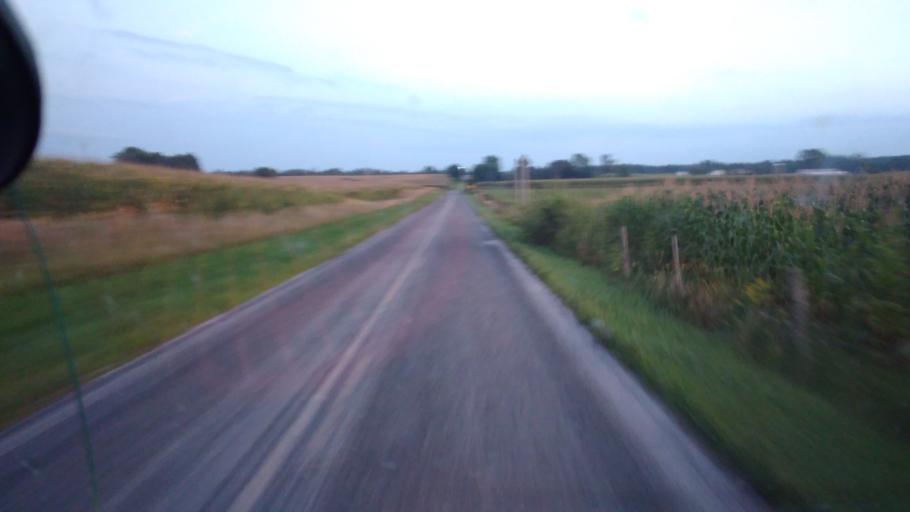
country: US
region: Ohio
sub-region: Hardin County
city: Kenton
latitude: 40.6255
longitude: -83.4571
